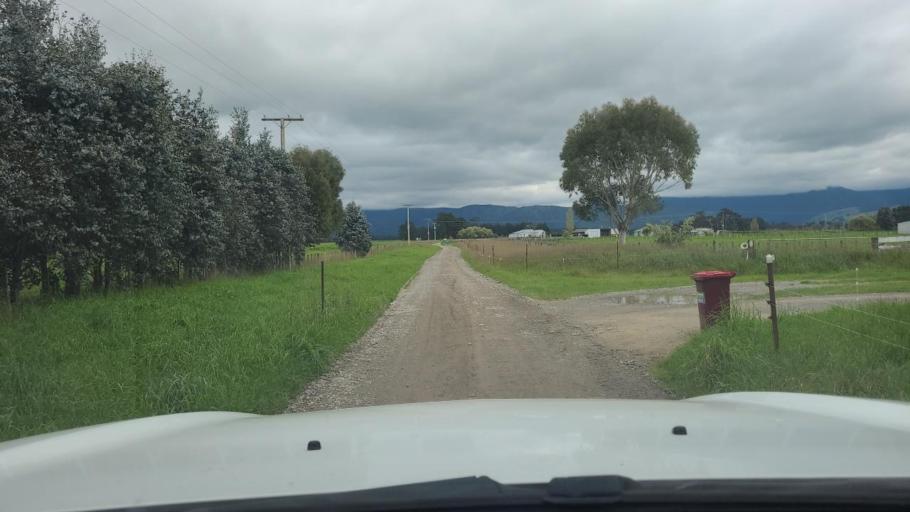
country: NZ
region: Wellington
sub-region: Masterton District
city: Masterton
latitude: -41.1266
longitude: 175.4225
